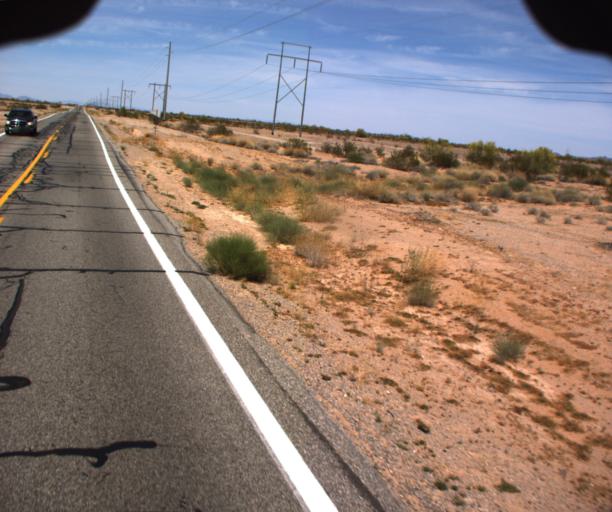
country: US
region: Arizona
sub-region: La Paz County
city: Quartzsite
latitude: 33.8197
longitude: -114.2170
